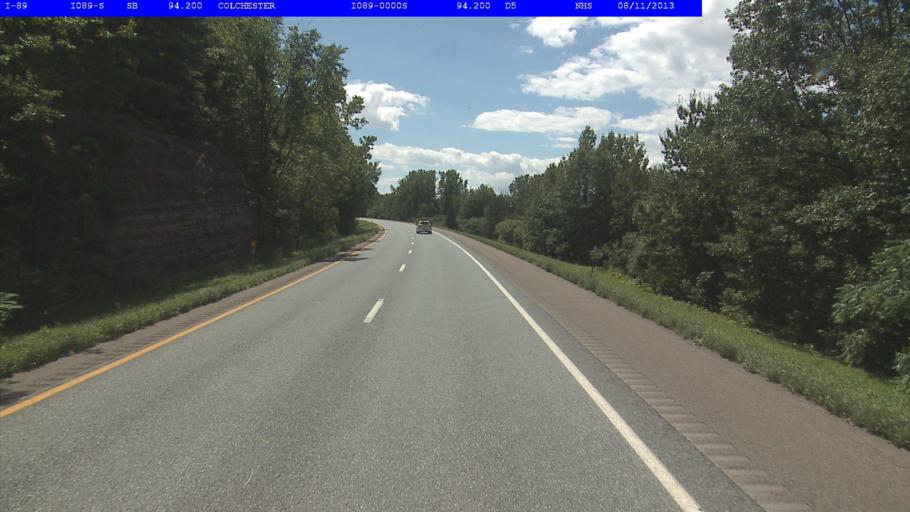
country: US
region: Vermont
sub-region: Chittenden County
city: Colchester
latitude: 44.5412
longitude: -73.1984
